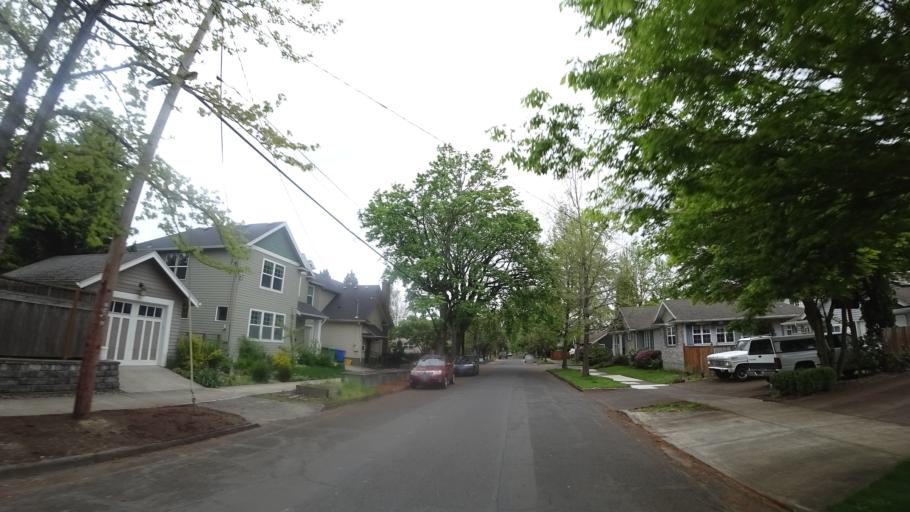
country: US
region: Oregon
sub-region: Clackamas County
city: Milwaukie
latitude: 45.4703
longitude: -122.6450
